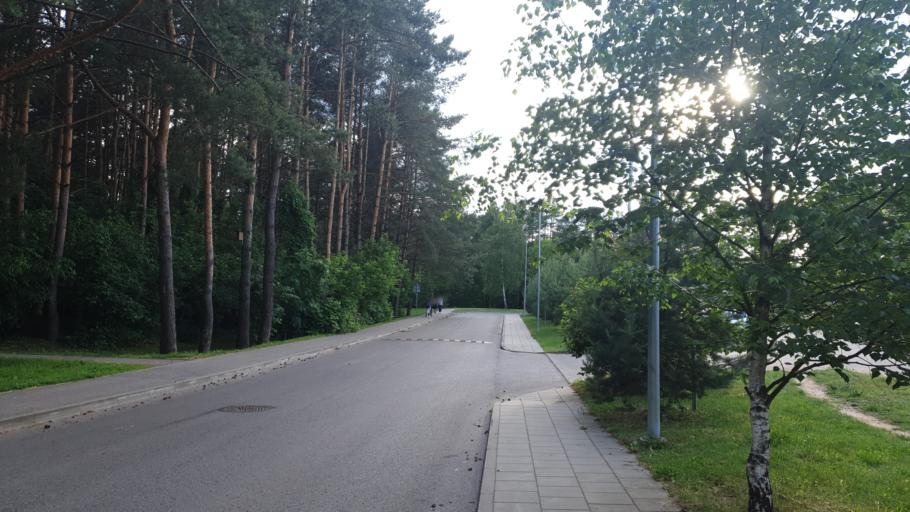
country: LT
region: Vilnius County
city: Rasos
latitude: 54.7263
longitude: 25.3186
